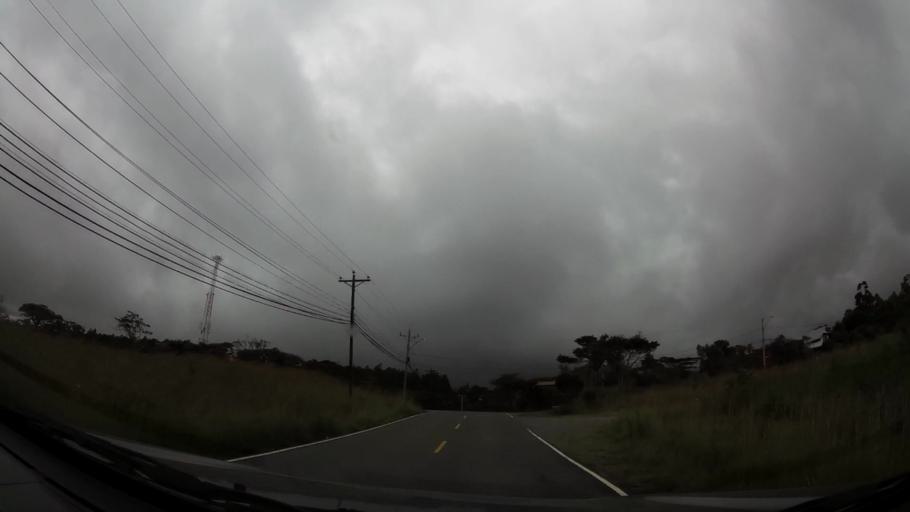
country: PA
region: Chiriqui
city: Palmira
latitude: 8.7386
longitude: -82.4387
